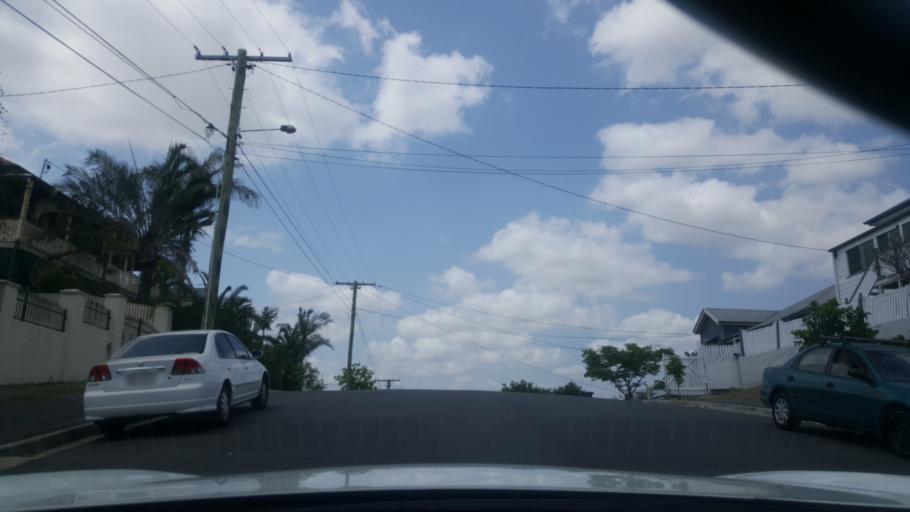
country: AU
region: Queensland
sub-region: Brisbane
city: South Brisbane
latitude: -27.4870
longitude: 153.0225
